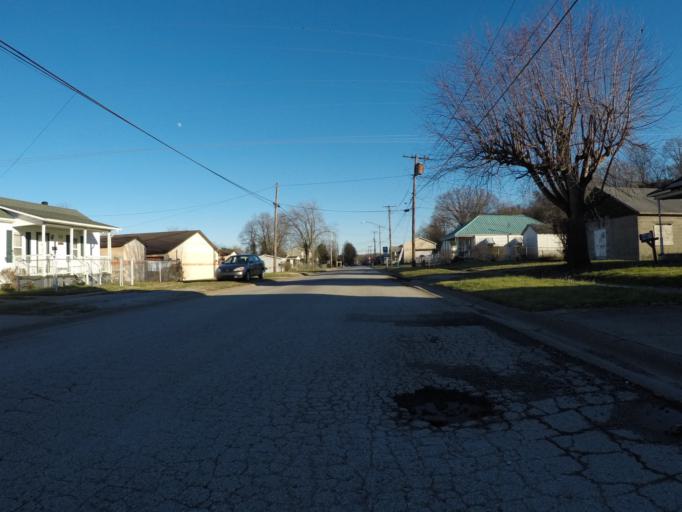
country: US
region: Kentucky
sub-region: Boyd County
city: Catlettsburg
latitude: 38.4012
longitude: -82.5910
